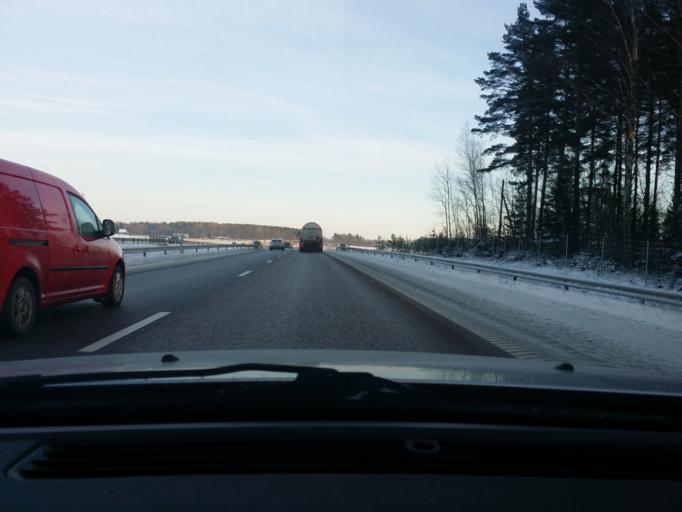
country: SE
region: OErebro
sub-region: Orebro Kommun
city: Hovsta
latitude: 59.3064
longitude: 15.3221
